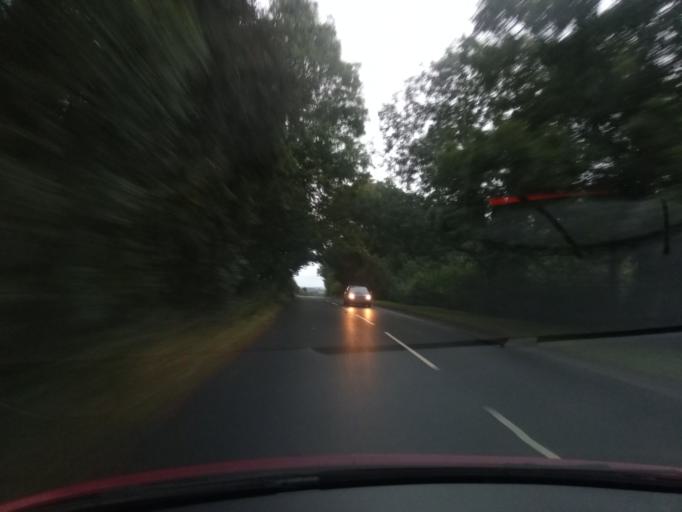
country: GB
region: England
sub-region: Darlington
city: Denton
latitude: 54.5426
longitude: -1.6734
